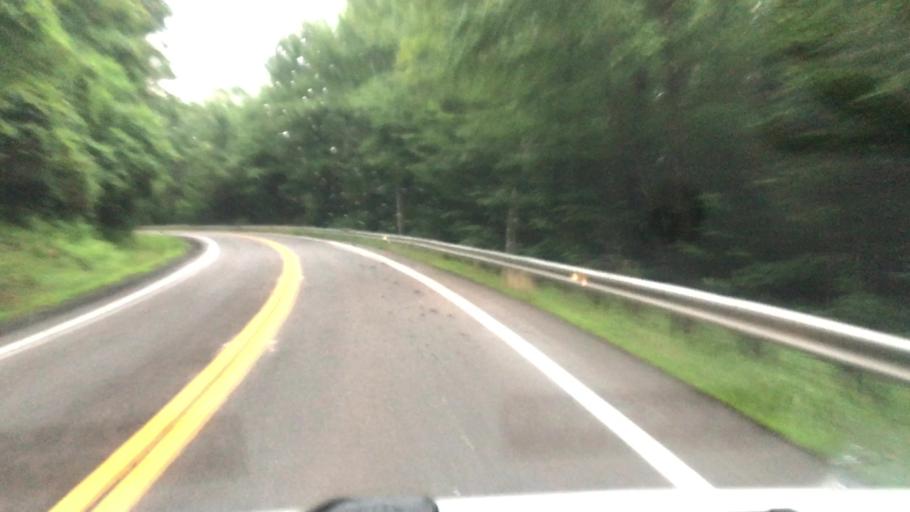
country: US
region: Massachusetts
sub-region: Hampshire County
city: Westhampton
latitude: 42.3049
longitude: -72.8611
